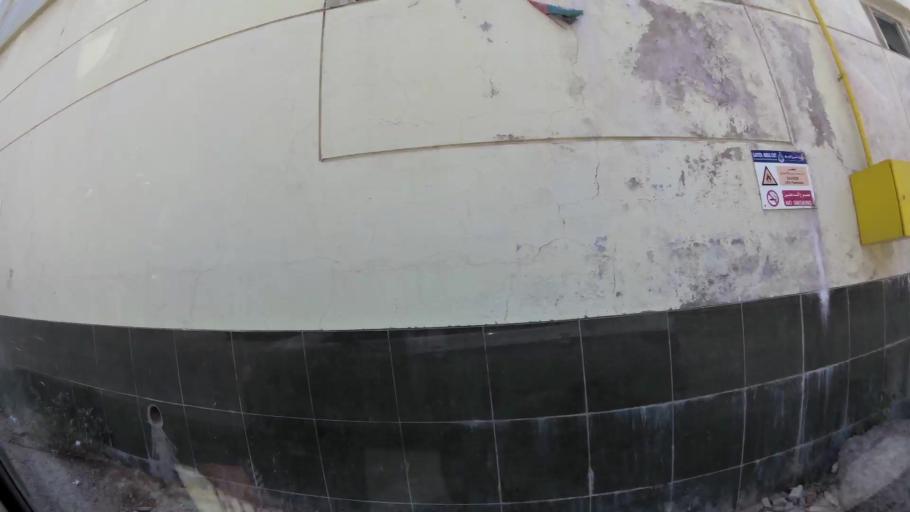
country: AE
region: Ash Shariqah
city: Sharjah
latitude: 25.2760
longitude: 55.4248
